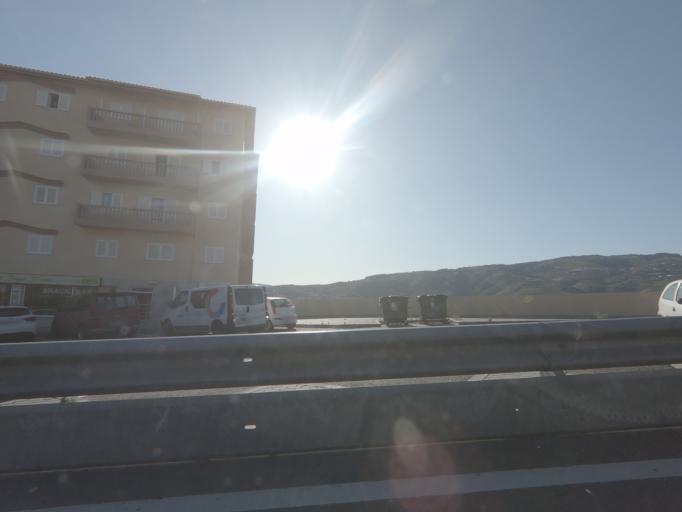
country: PT
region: Vila Real
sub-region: Santa Marta de Penaguiao
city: Santa Marta de Penaguiao
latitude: 41.1971
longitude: -7.8029
